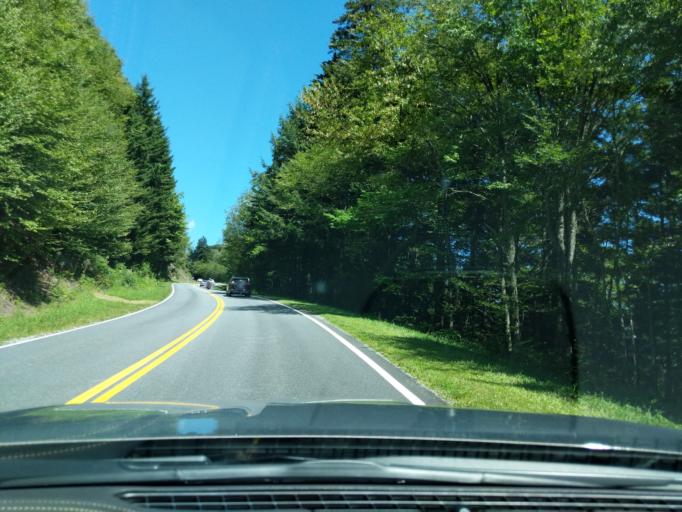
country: US
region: Tennessee
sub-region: Sevier County
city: Gatlinburg
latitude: 35.6091
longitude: -83.4323
